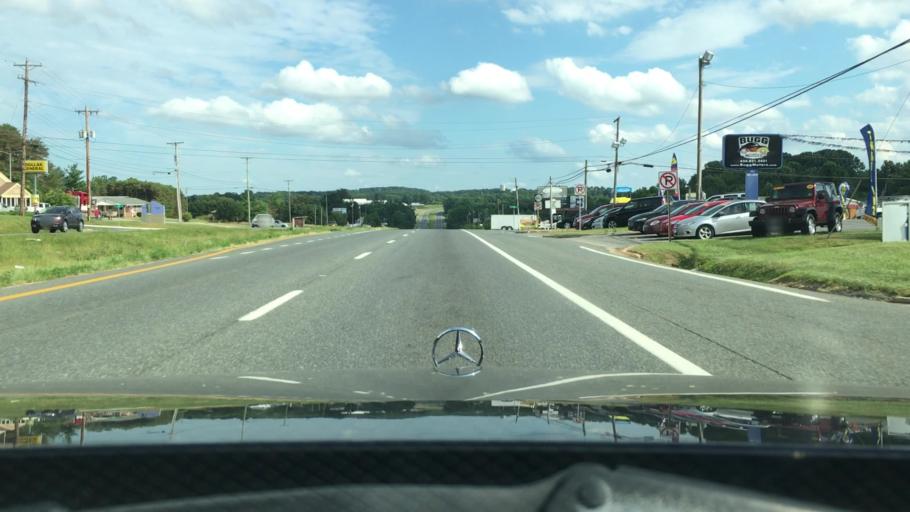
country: US
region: Virginia
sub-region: Campbell County
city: Rustburg
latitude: 37.2978
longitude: -79.1726
